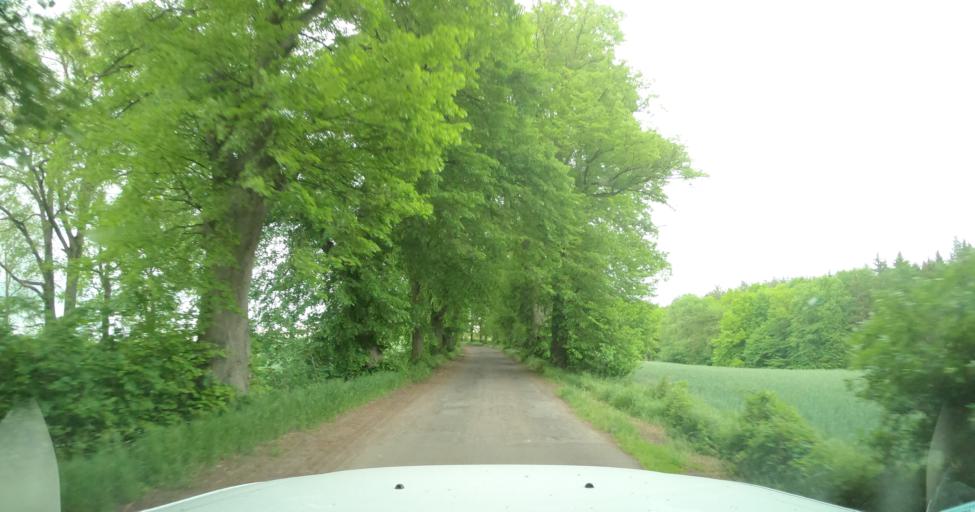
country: PL
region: West Pomeranian Voivodeship
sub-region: Powiat stargardzki
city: Dolice
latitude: 53.2438
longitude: 15.2472
